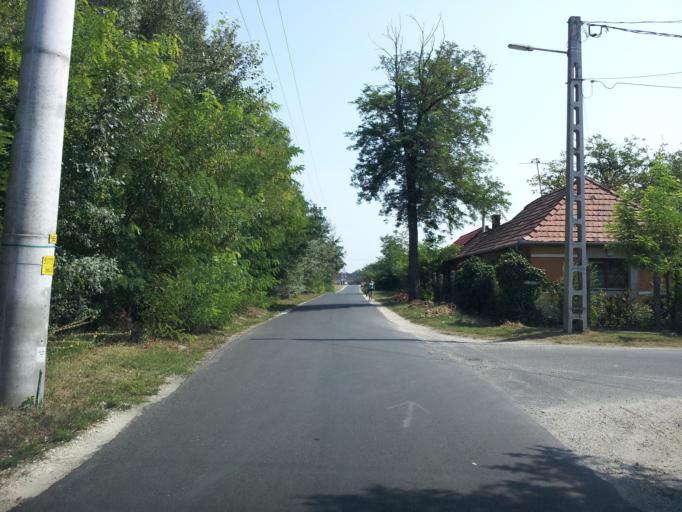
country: HU
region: Pest
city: Dunavarsany
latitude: 47.2847
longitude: 19.0593
